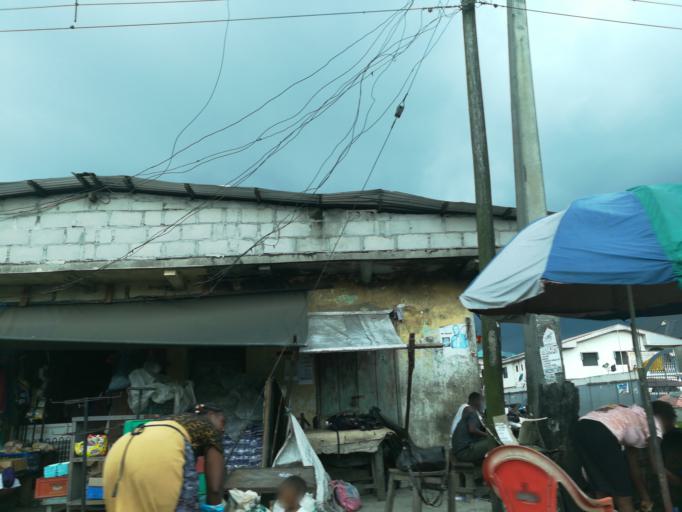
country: NG
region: Rivers
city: Port Harcourt
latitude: 4.7942
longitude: 6.9864
